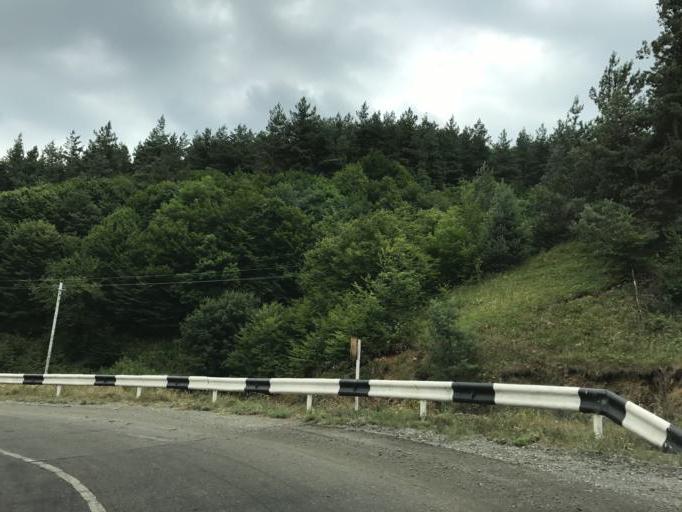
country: AZ
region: Susa
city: Shushi
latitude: 39.6975
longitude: 46.6502
